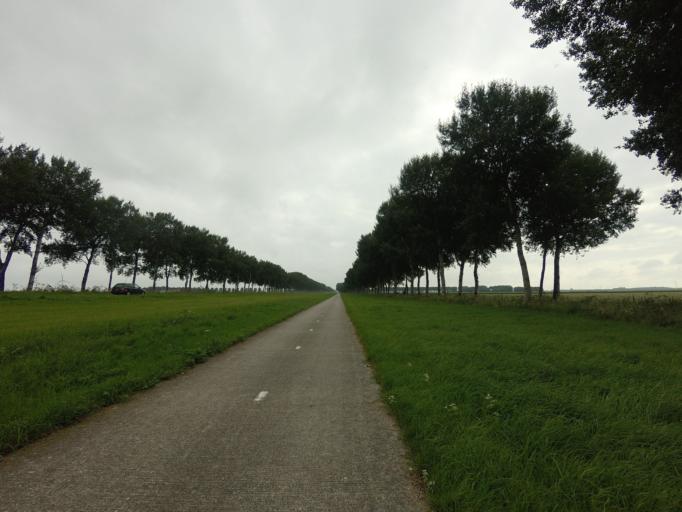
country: NL
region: Flevoland
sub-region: Gemeente Zeewolde
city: Zeewolde
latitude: 52.3838
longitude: 5.4295
